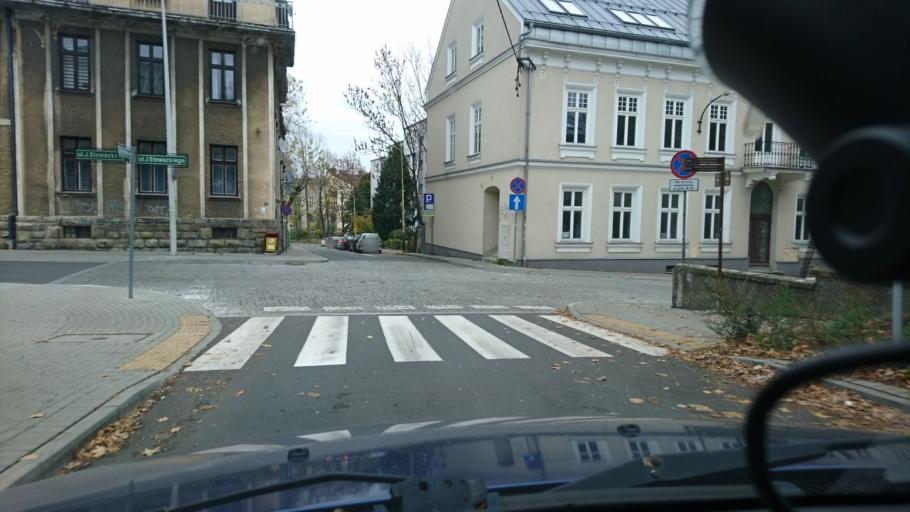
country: PL
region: Silesian Voivodeship
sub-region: Bielsko-Biala
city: Bielsko-Biala
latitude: 49.8235
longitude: 19.0418
